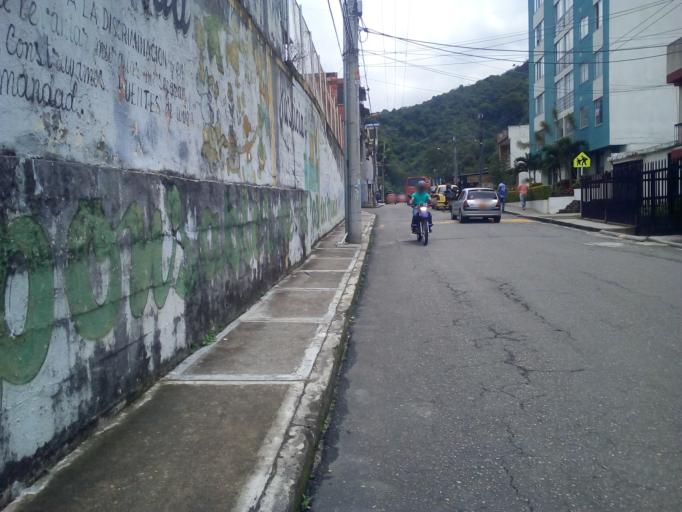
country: CO
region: Tolima
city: Ibague
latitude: 4.4521
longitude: -75.2441
